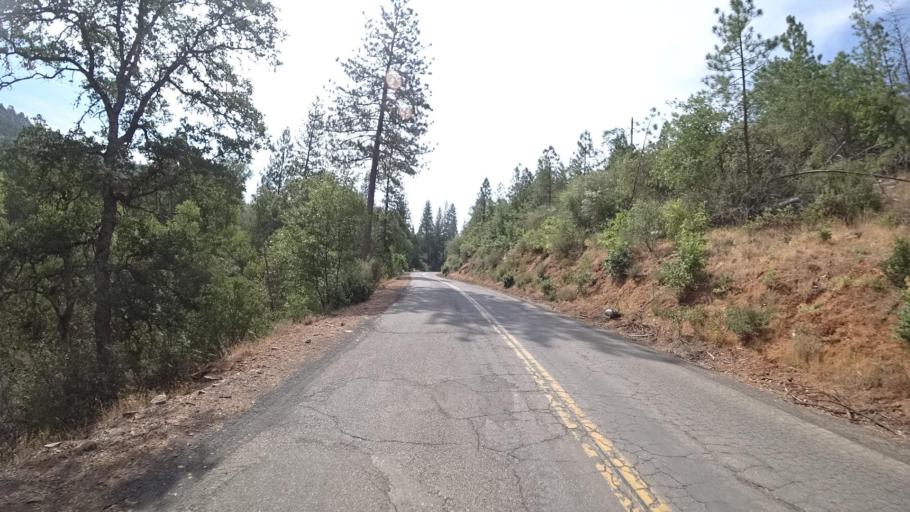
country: US
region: California
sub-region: Mariposa County
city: Mariposa
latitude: 37.5480
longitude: -119.9966
